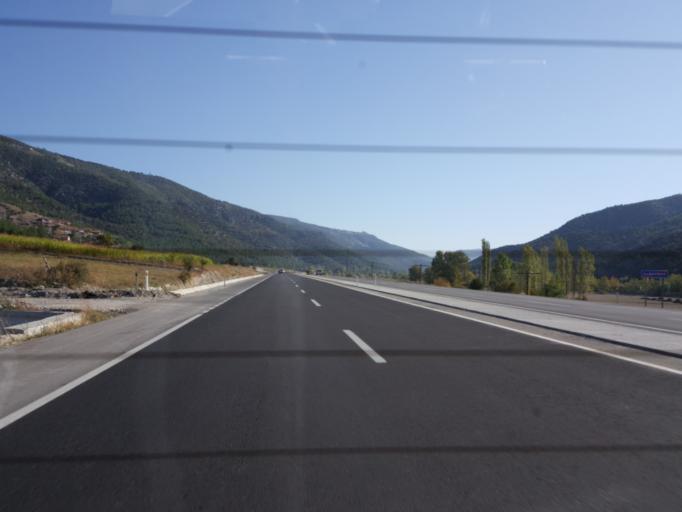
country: TR
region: Tokat
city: Turhal
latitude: 40.4646
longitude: 36.1180
